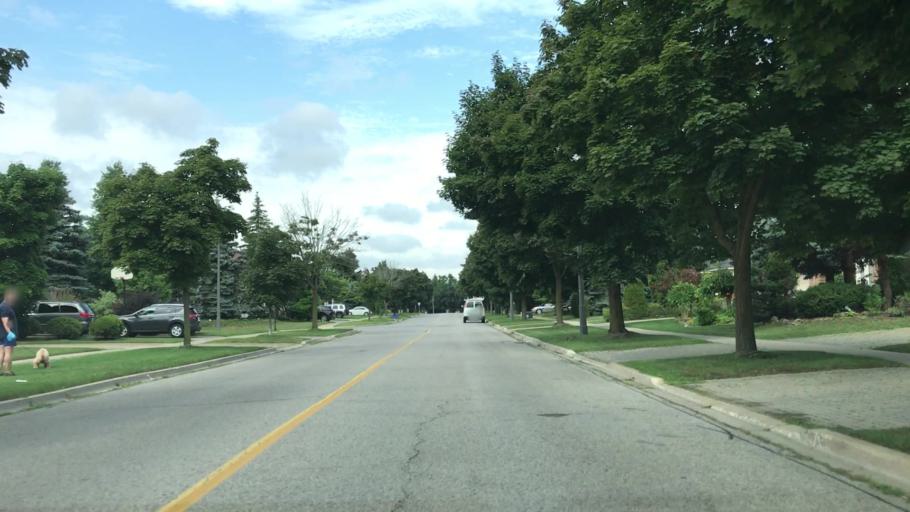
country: CA
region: Ontario
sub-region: York
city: Richmond Hill
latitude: 43.8632
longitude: -79.4003
